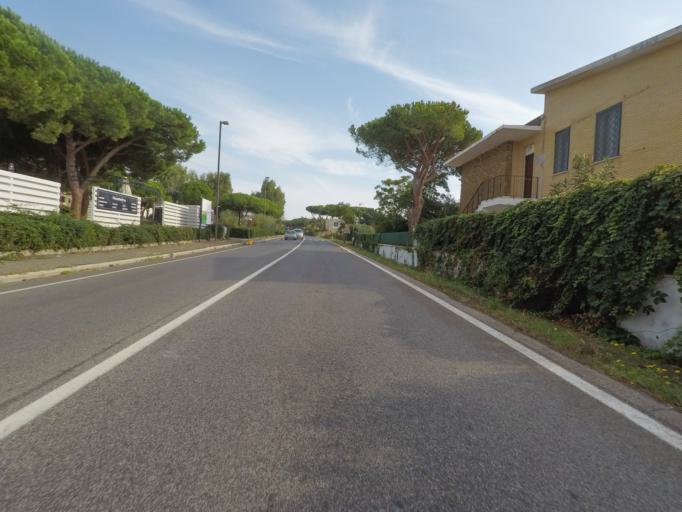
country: IT
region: Latium
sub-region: Citta metropolitana di Roma Capitale
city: Santa Marinella
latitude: 42.0345
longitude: 11.8347
